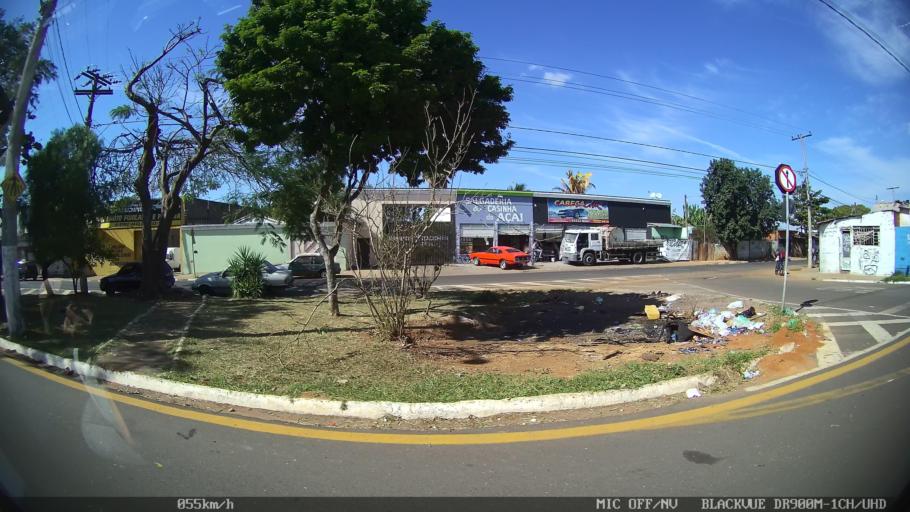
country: BR
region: Sao Paulo
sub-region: Franca
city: Franca
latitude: -20.5009
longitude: -47.3983
